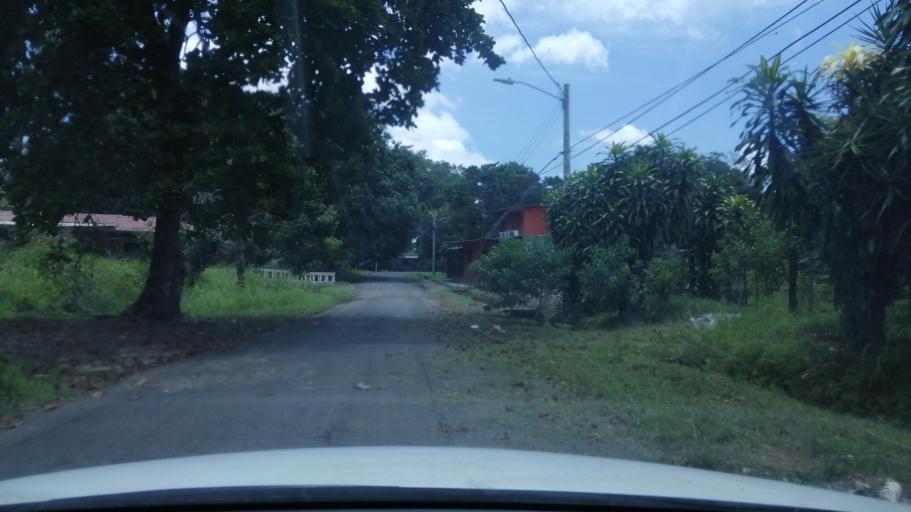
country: PA
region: Chiriqui
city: David
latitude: 8.4240
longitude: -82.4396
